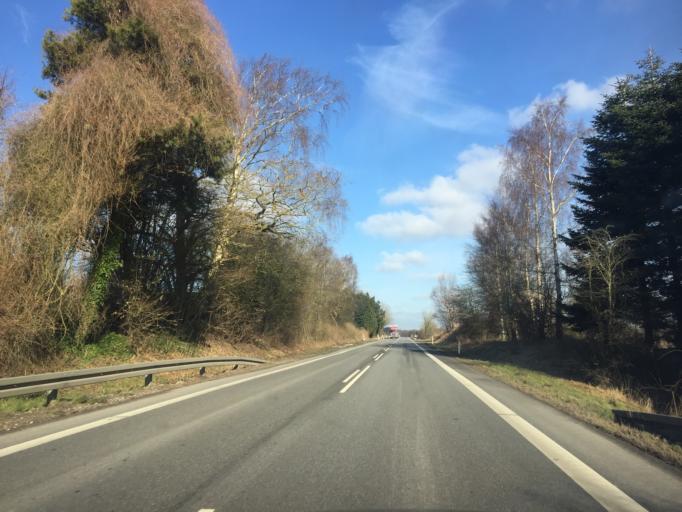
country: DK
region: South Denmark
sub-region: Assens Kommune
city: Vissenbjerg
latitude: 55.4226
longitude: 10.1790
